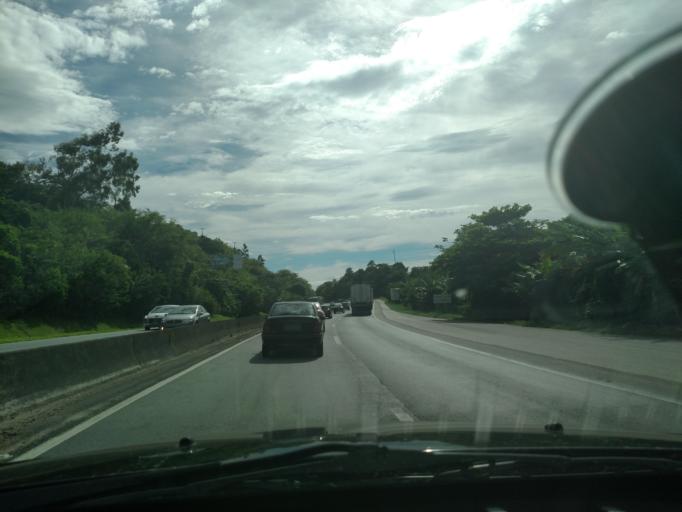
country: BR
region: Santa Catarina
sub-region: Biguacu
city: Biguacu
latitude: -27.4792
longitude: -48.6443
